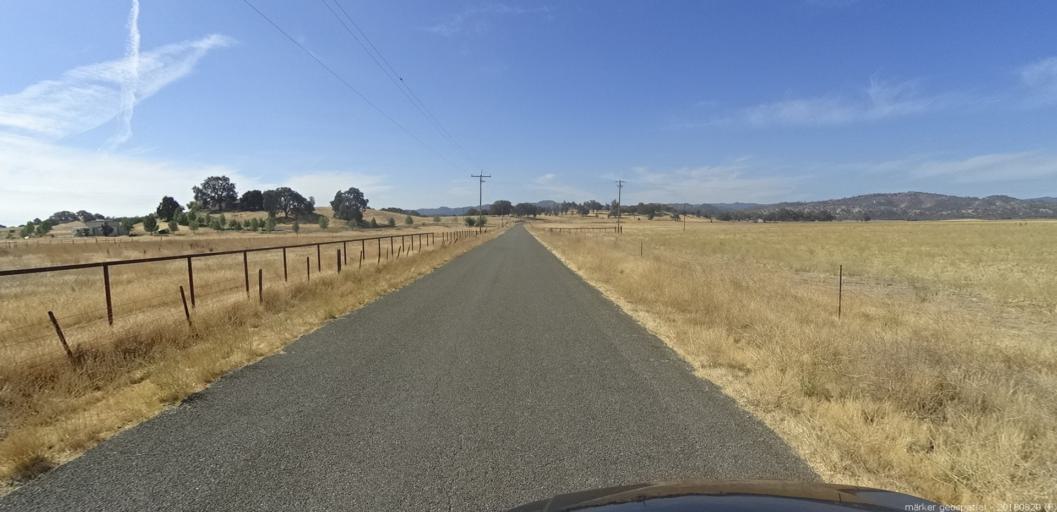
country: US
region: California
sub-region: Monterey County
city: King City
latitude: 35.9457
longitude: -121.1179
